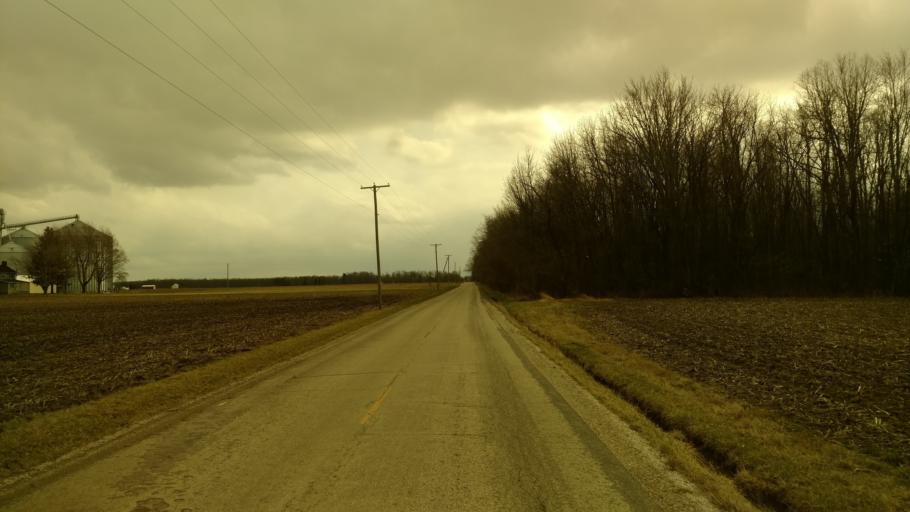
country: US
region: Ohio
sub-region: Crawford County
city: Crestline
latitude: 40.8096
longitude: -82.6971
